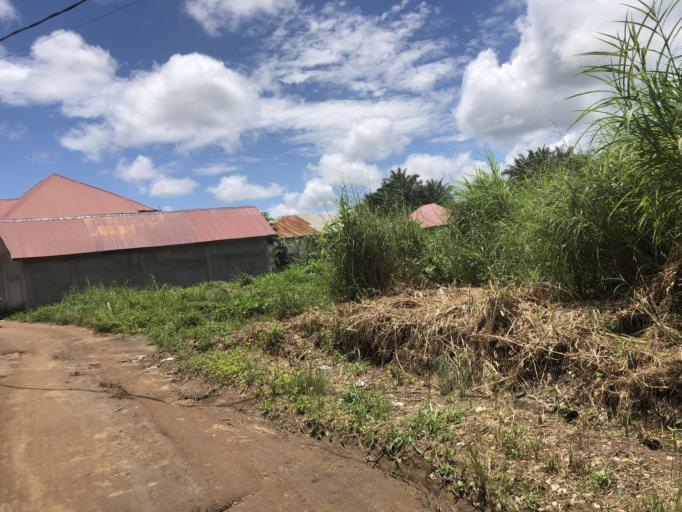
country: SL
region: Northern Province
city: Makeni
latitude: 8.8582
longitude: -12.0479
